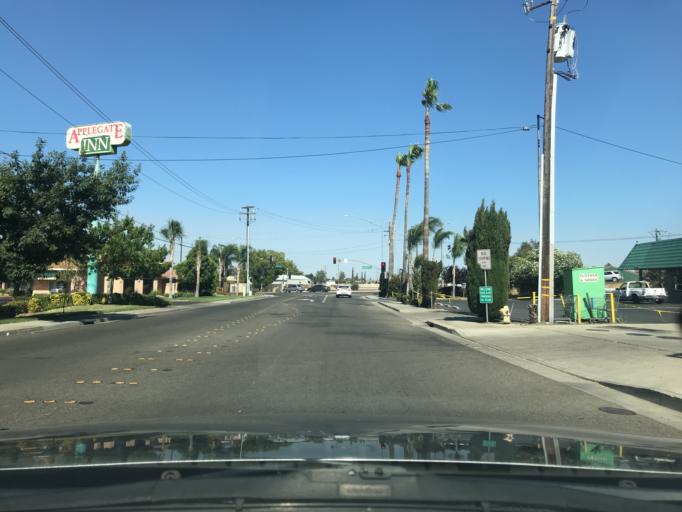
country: US
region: California
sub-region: Merced County
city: Atwater
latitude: 37.3457
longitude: -120.6137
